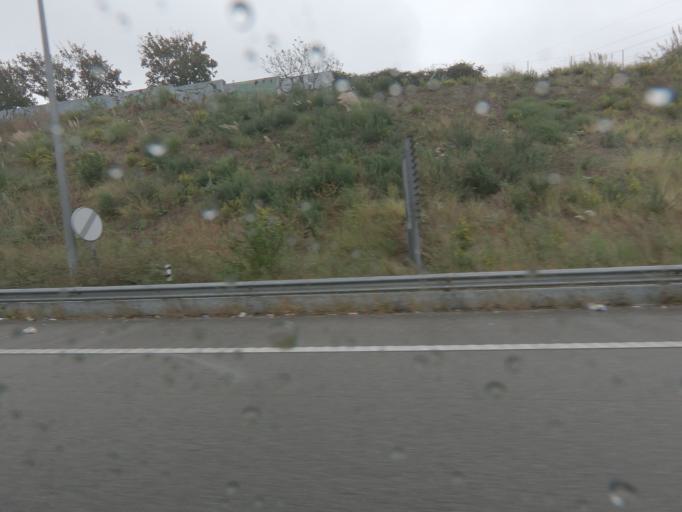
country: PT
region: Porto
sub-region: Matosinhos
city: Guifoes
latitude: 41.1947
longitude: -8.6654
